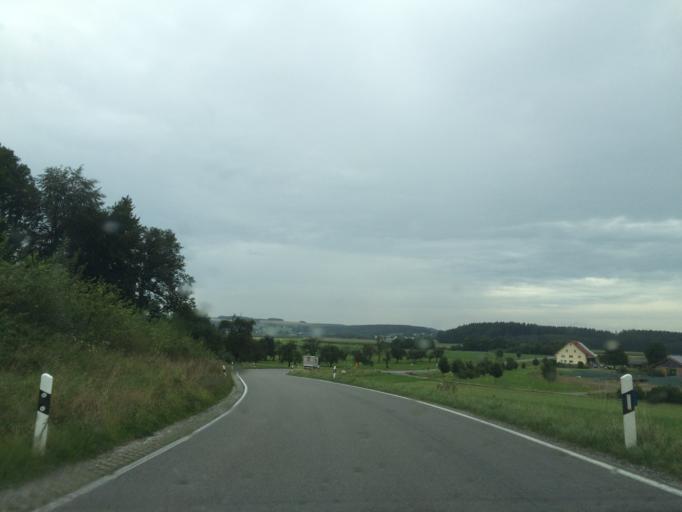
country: DE
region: Baden-Wuerttemberg
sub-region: Tuebingen Region
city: Bad Waldsee
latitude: 47.9543
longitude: 9.7868
